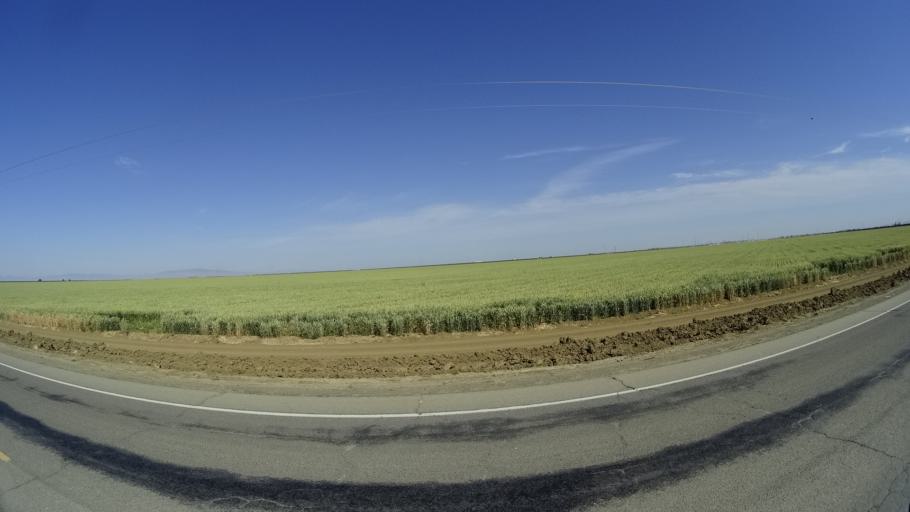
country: US
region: California
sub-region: Kings County
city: Lemoore Station
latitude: 36.2123
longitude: -119.9161
